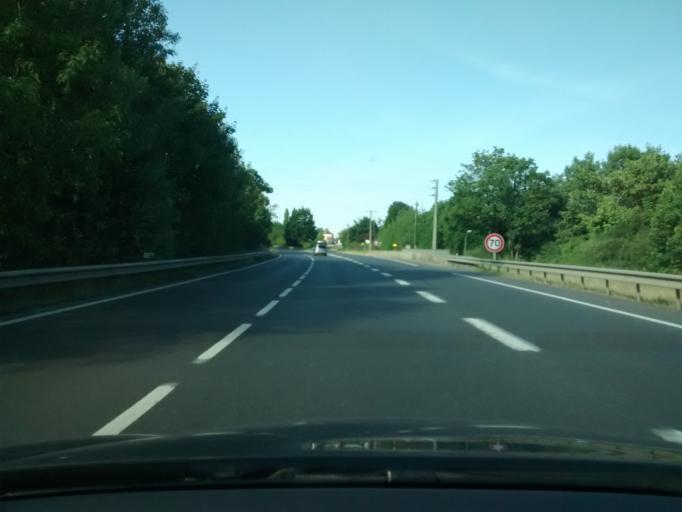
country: FR
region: Ile-de-France
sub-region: Departement de l'Essonne
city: Saclay
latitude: 48.7340
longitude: 2.1696
